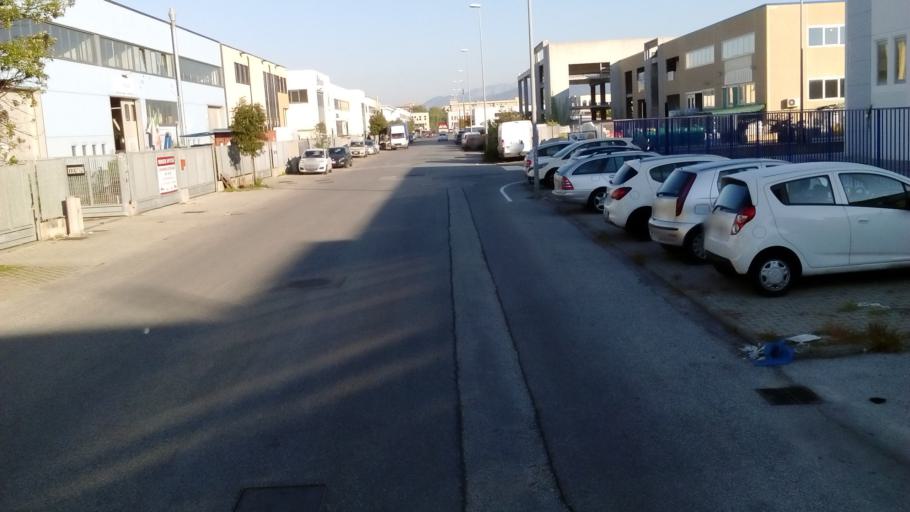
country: IT
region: Tuscany
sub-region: Provincia di Lucca
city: Viareggio
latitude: 43.8579
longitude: 10.2751
